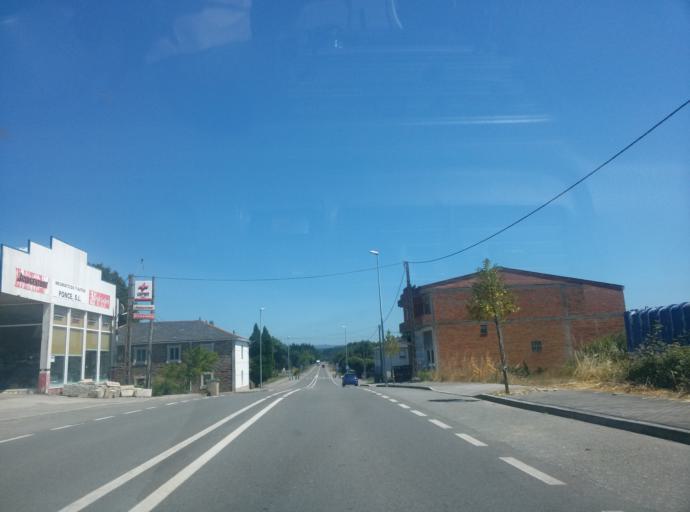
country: ES
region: Galicia
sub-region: Provincia de Lugo
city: Castro de Rei
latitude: 43.2513
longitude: -7.4250
